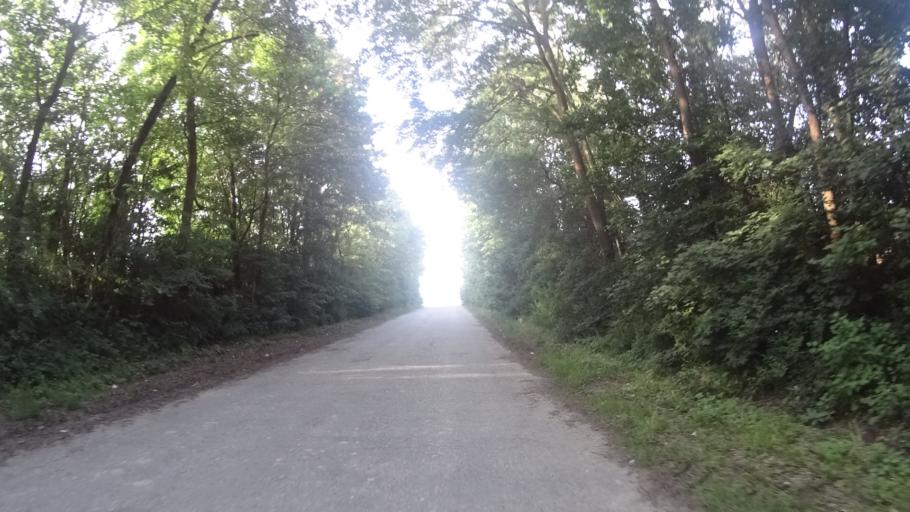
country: DE
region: Baden-Wuerttemberg
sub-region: Freiburg Region
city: Hartheim
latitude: 47.9470
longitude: 7.6474
